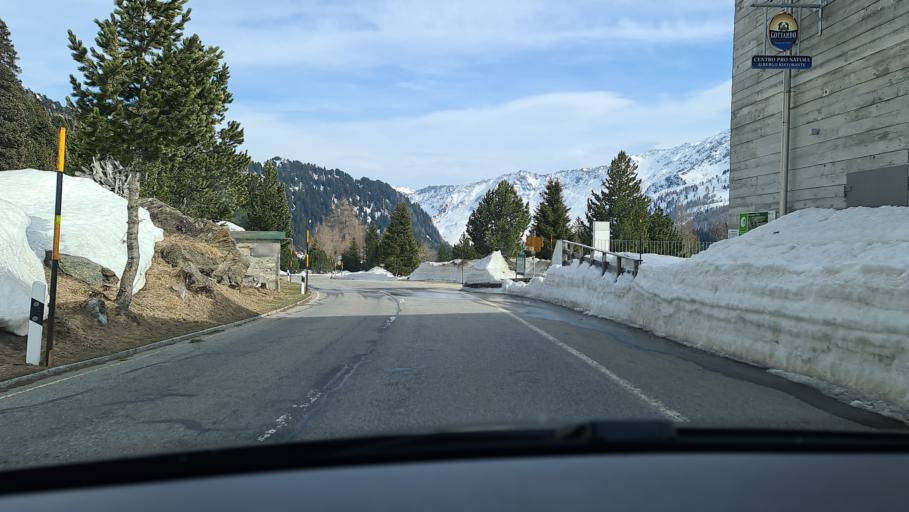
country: CH
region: Ticino
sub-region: Leventina District
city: Faido
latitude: 46.5378
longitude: 8.8340
